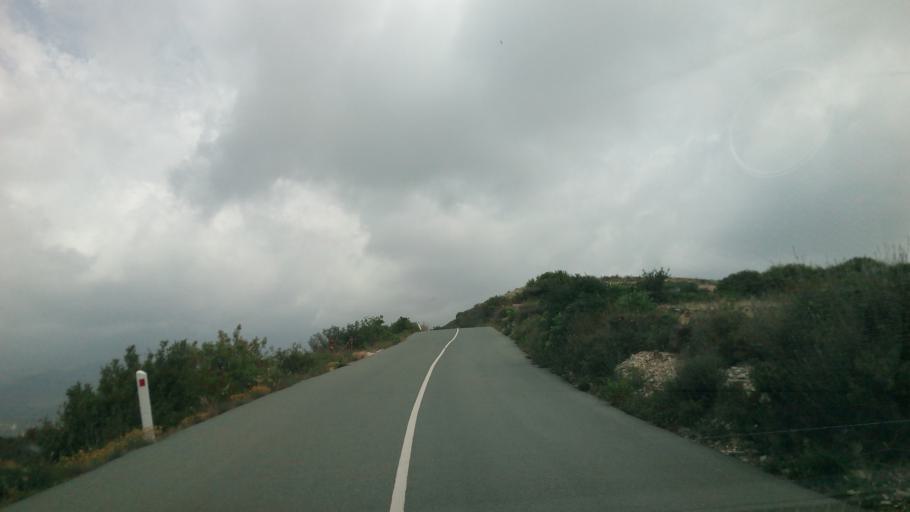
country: CY
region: Limassol
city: Pachna
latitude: 34.8328
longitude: 32.8687
